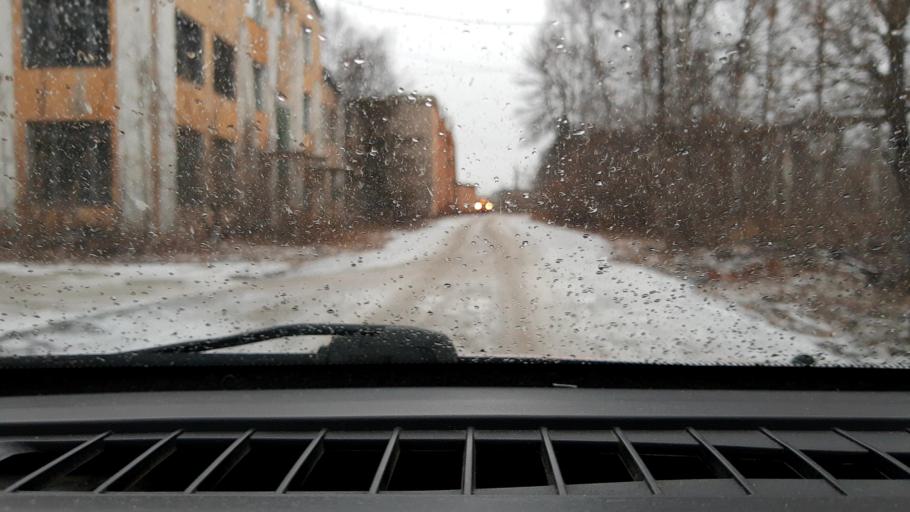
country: RU
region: Nizjnij Novgorod
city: Nizhniy Novgorod
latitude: 56.2656
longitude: 43.9340
